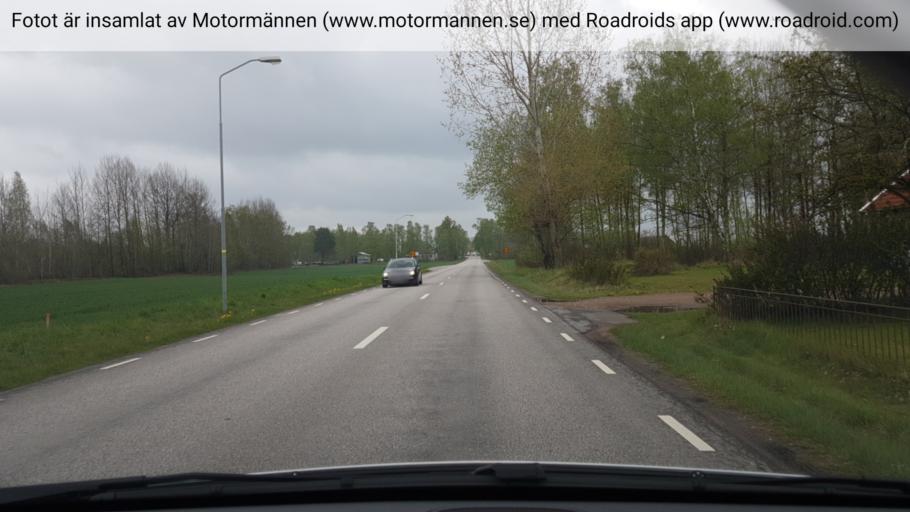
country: SE
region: Vaestra Goetaland
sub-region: Skovde Kommun
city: Stopen
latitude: 58.5590
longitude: 14.0078
